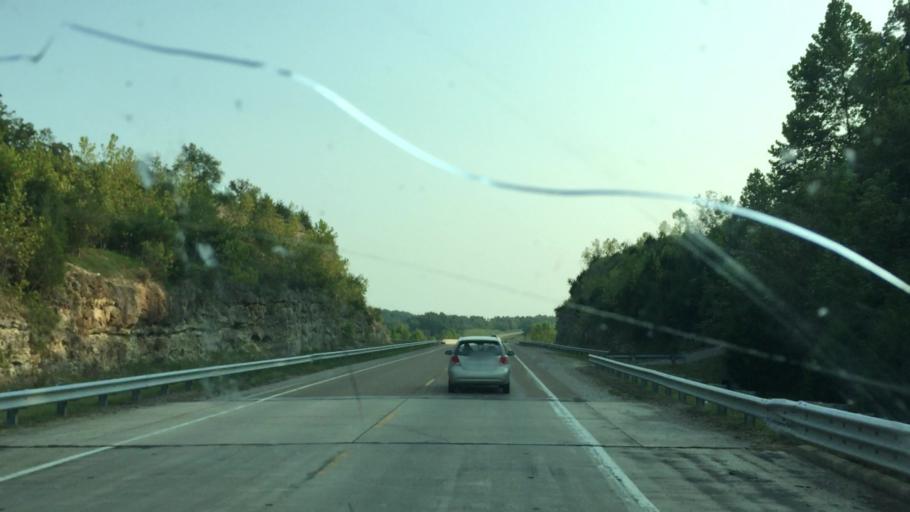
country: US
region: Missouri
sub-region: Pulaski County
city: Richland
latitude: 37.8001
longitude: -92.4055
